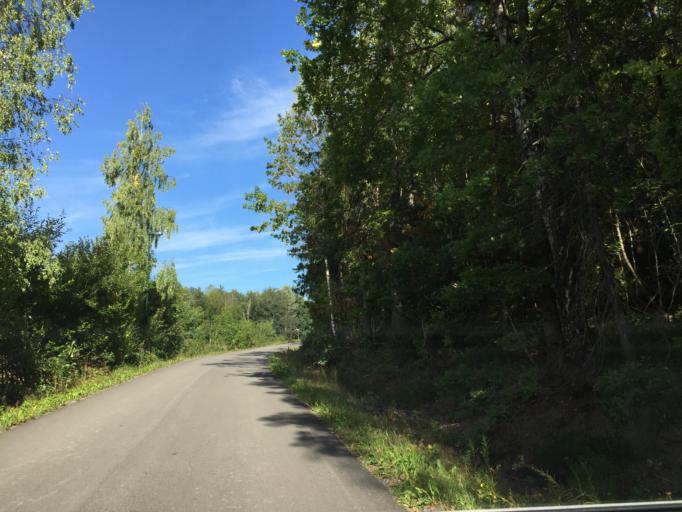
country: NO
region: Vestfold
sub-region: Holmestrand
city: Gullhaug
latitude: 59.4841
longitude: 10.1714
